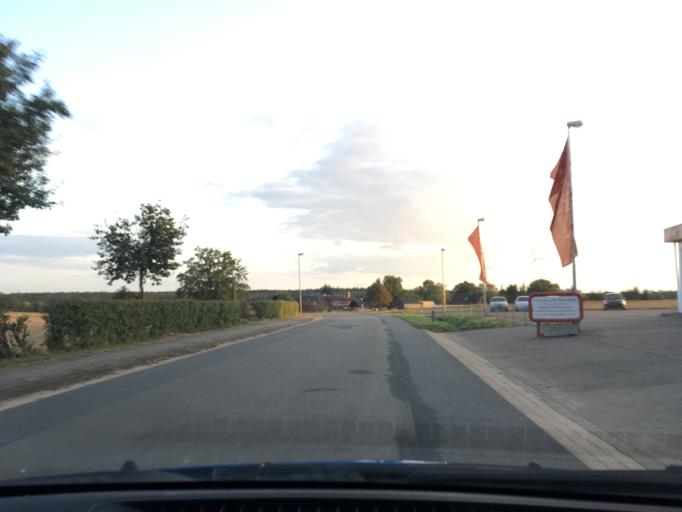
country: DE
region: Lower Saxony
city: Tosterglope
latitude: 53.2091
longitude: 10.8175
